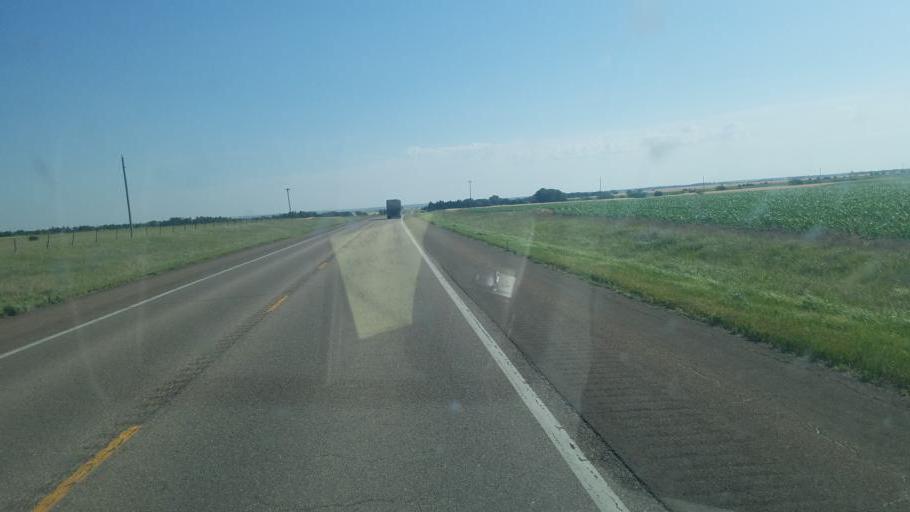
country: US
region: Kansas
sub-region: Barton County
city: Great Bend
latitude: 38.3967
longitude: -98.6723
